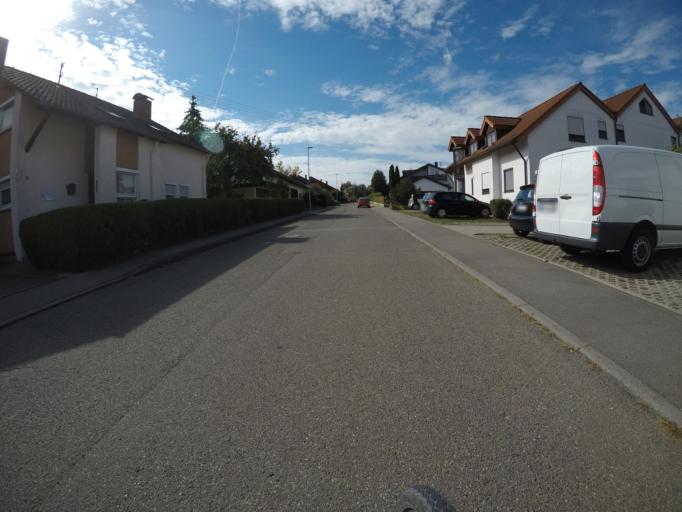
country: DE
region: Baden-Wuerttemberg
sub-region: Regierungsbezirk Stuttgart
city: Hildrizhausen
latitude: 48.6246
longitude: 8.9627
